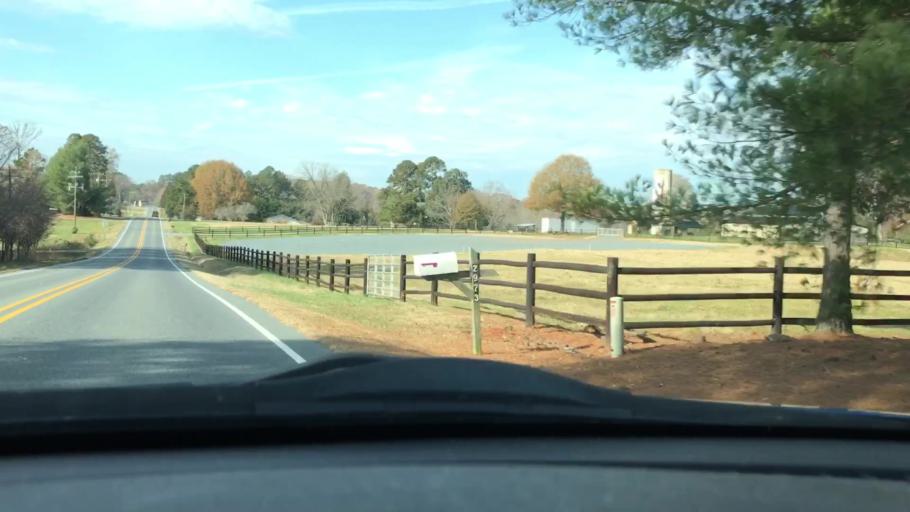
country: US
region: North Carolina
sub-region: Randolph County
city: Asheboro
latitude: 35.6742
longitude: -79.8983
